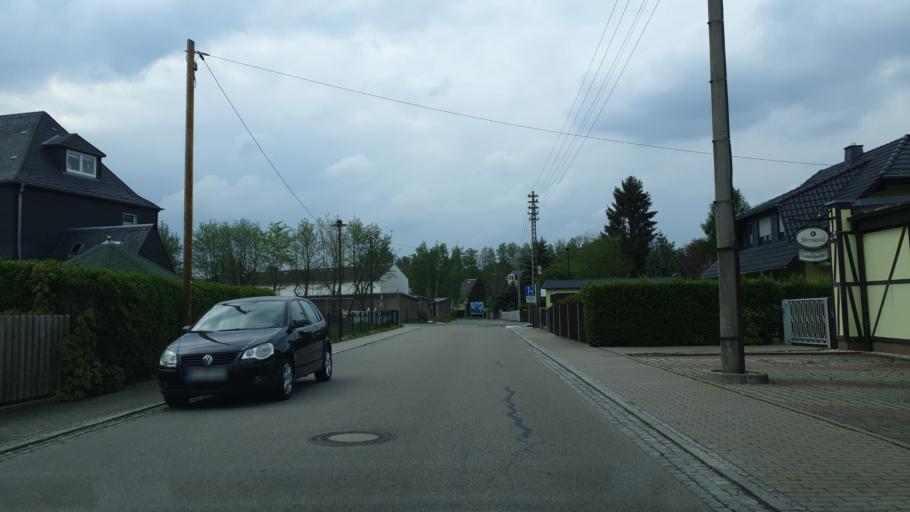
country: DE
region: Saxony
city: Oberlungwitz
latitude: 50.7812
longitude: 12.7096
